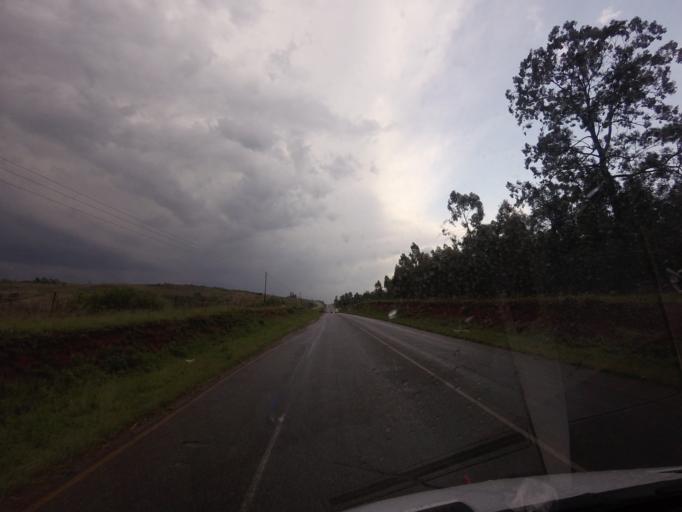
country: SZ
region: Hhohho
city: Lobamba
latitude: -26.5090
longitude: 31.2543
